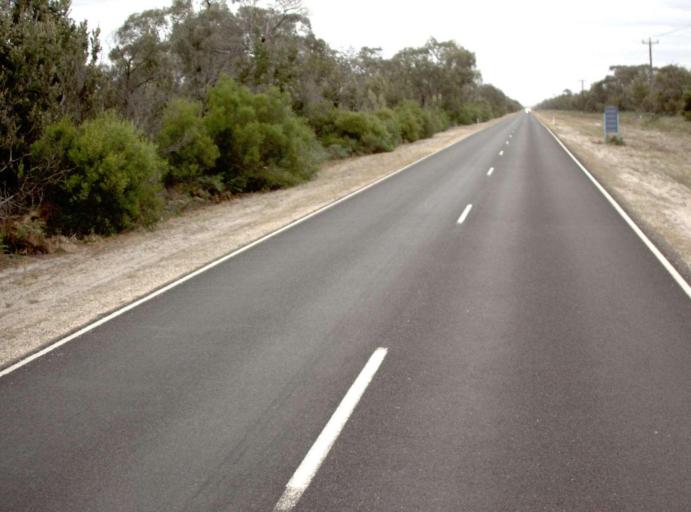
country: AU
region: Victoria
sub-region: East Gippsland
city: Bairnsdale
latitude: -38.0665
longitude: 147.5550
